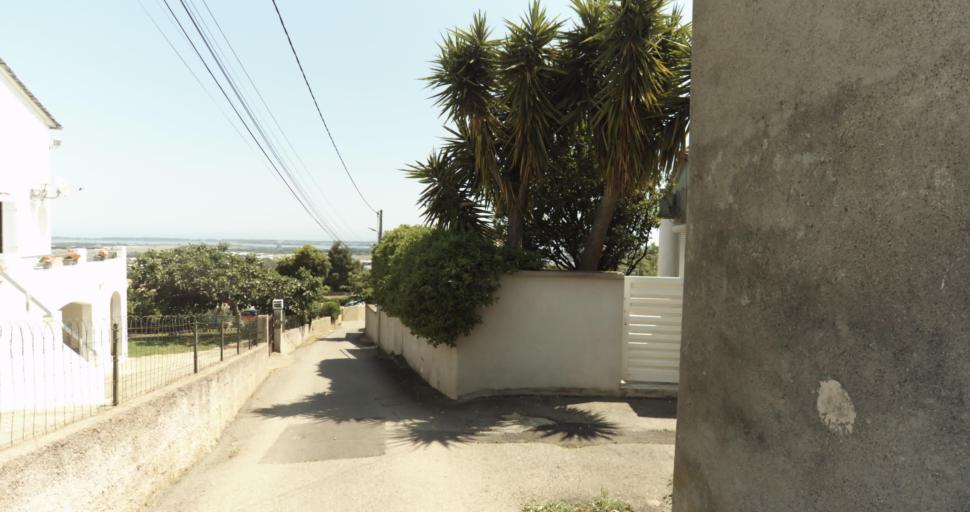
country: FR
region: Corsica
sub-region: Departement de la Haute-Corse
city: Biguglia
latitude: 42.5933
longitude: 9.4268
